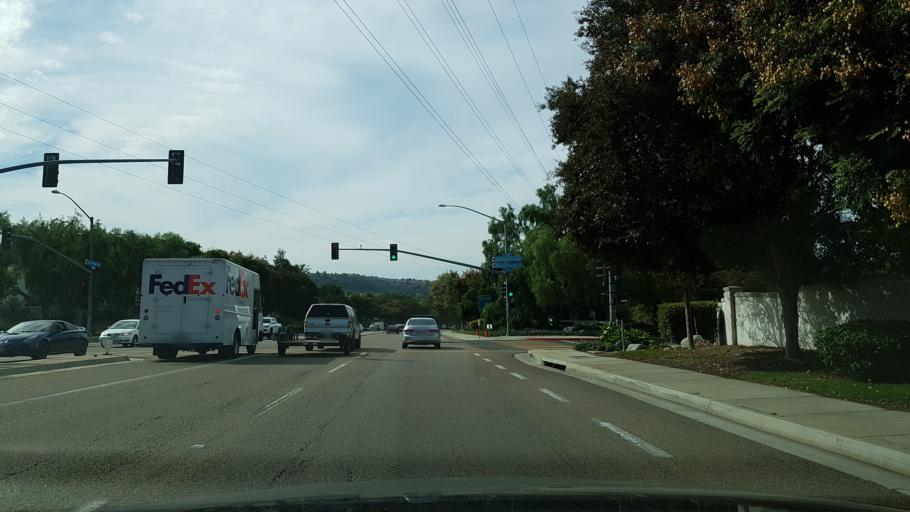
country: US
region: California
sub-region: San Diego County
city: Poway
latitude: 32.9343
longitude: -117.0838
